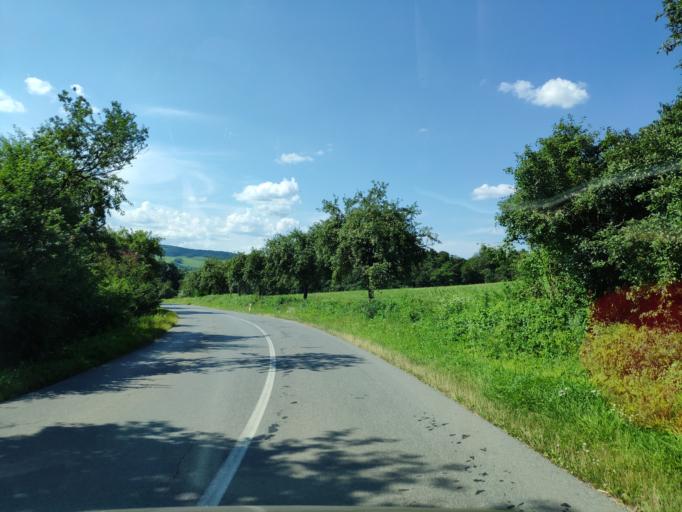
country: SK
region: Presovsky
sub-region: Okres Presov
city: Presov
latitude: 48.8875
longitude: 21.2635
